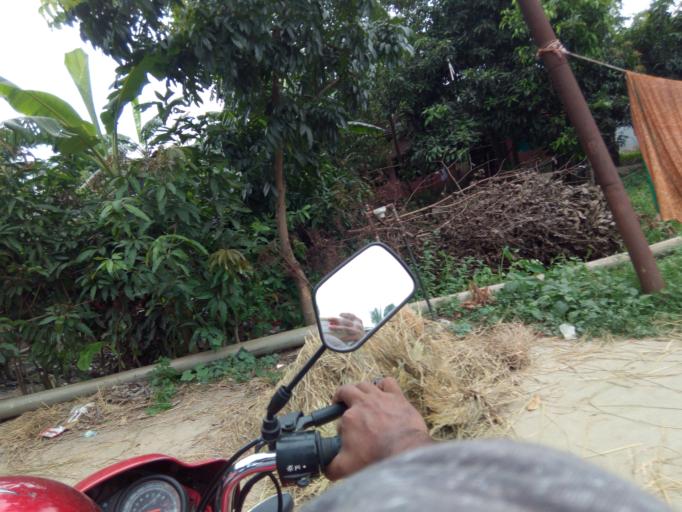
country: BD
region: Dhaka
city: Paltan
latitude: 23.7462
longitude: 90.4851
